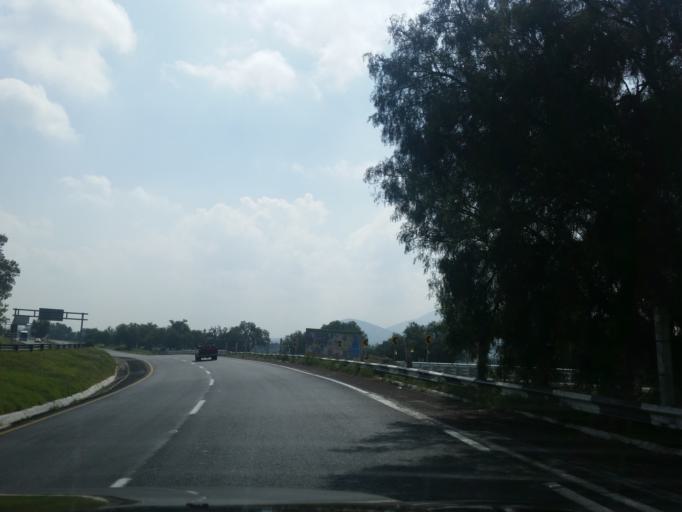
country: MX
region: Mexico
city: Acolman
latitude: 19.6288
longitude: -98.9136
